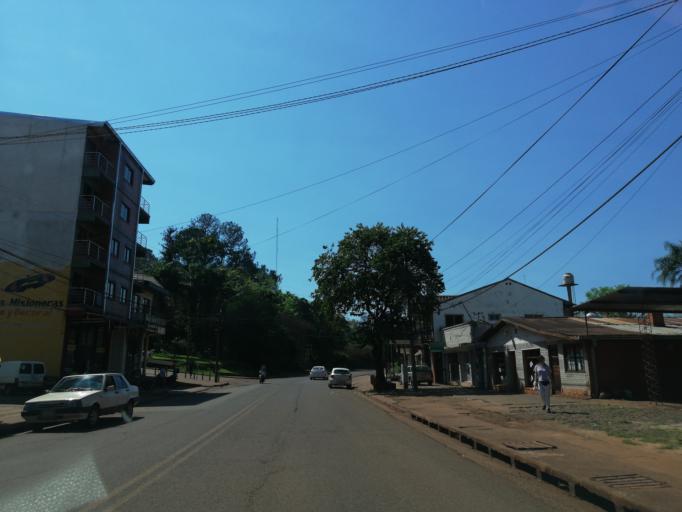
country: AR
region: Misiones
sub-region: Departamento de Eldorado
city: Eldorado
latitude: -26.4057
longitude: -54.6143
